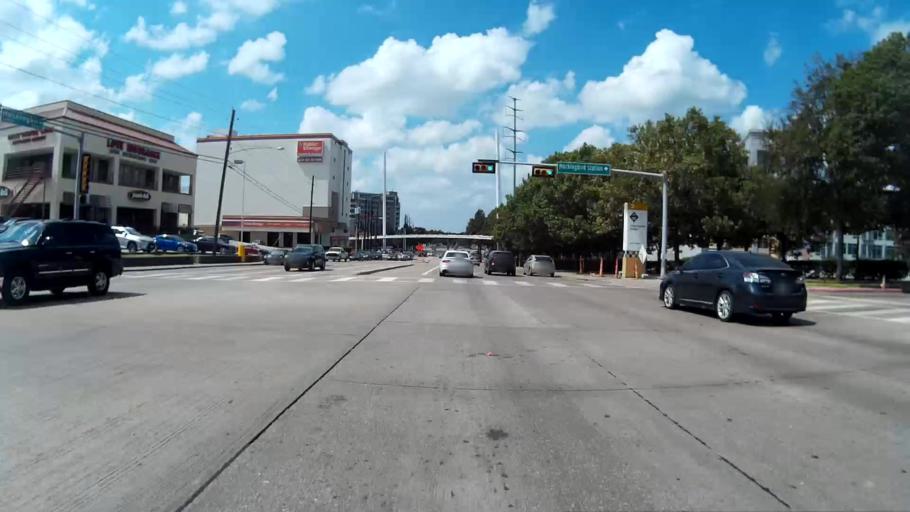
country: US
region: Texas
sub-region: Dallas County
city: Highland Park
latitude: 32.8366
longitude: -96.7752
